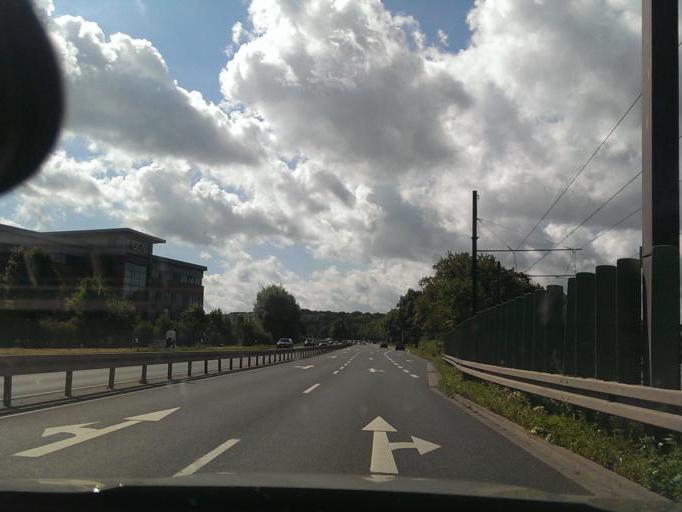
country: DE
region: Lower Saxony
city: Sarstedt
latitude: 52.2551
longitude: 9.8594
